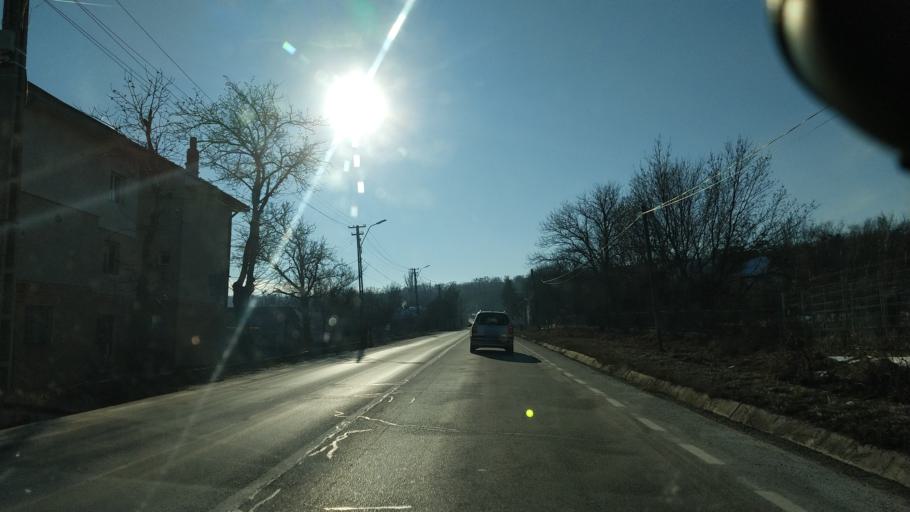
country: RO
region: Iasi
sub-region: Comuna Strunga
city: Strunga
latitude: 47.1696
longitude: 26.9539
